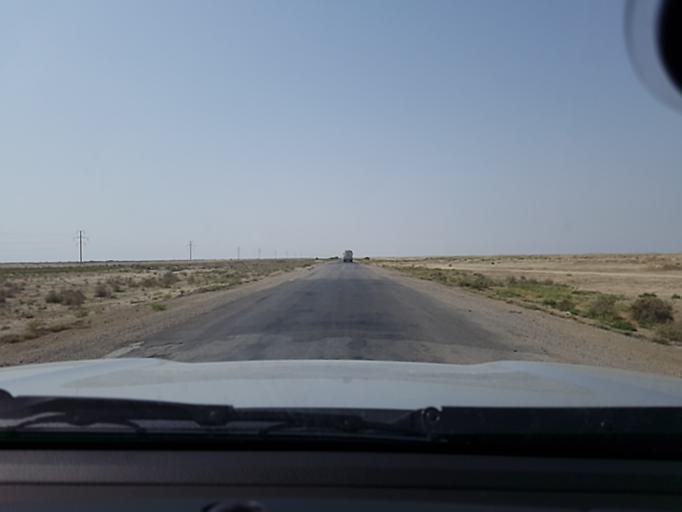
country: TM
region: Balkan
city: Gumdag
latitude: 38.8628
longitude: 54.5946
